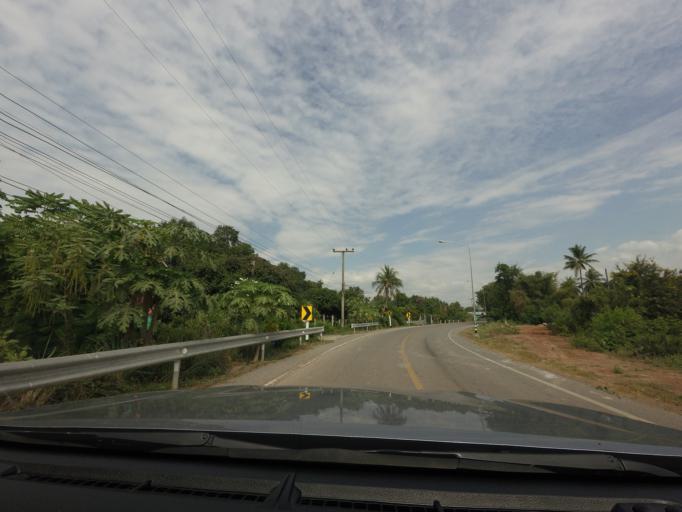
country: TH
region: Phitsanulok
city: Wang Thong
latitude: 16.7309
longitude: 100.3780
